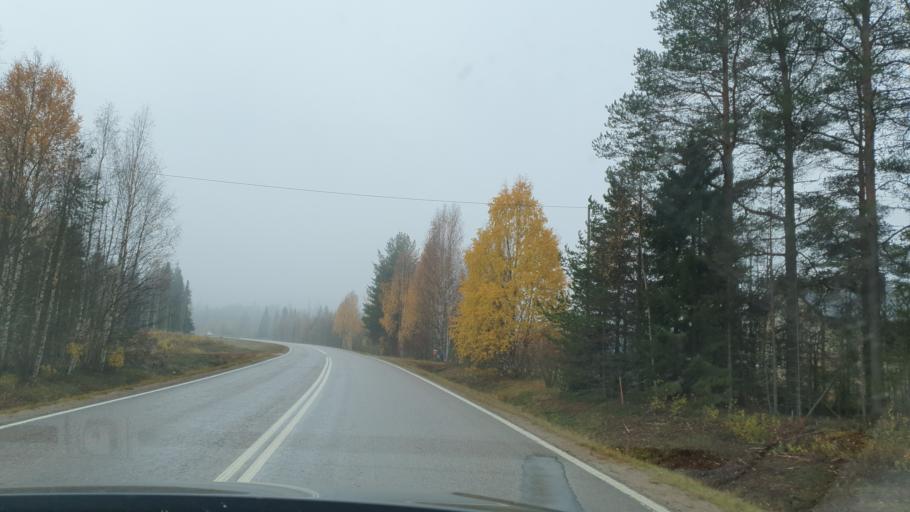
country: FI
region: Lapland
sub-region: Rovaniemi
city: Rovaniemi
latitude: 66.8185
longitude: 25.3950
